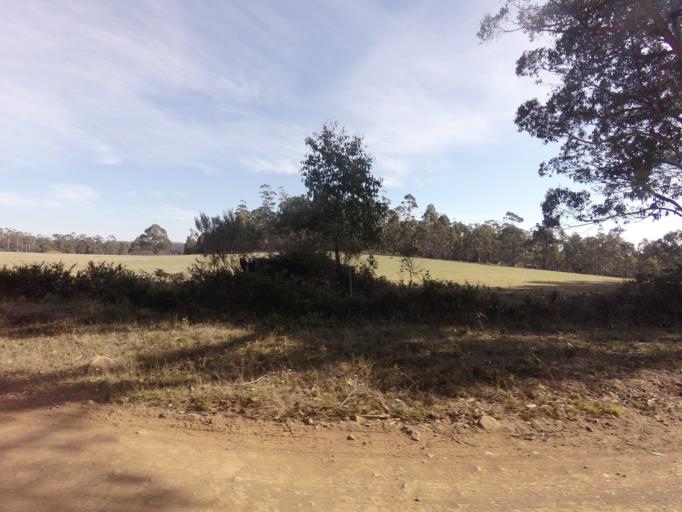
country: AU
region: Tasmania
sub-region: Sorell
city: Sorell
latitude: -42.4853
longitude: 147.4906
